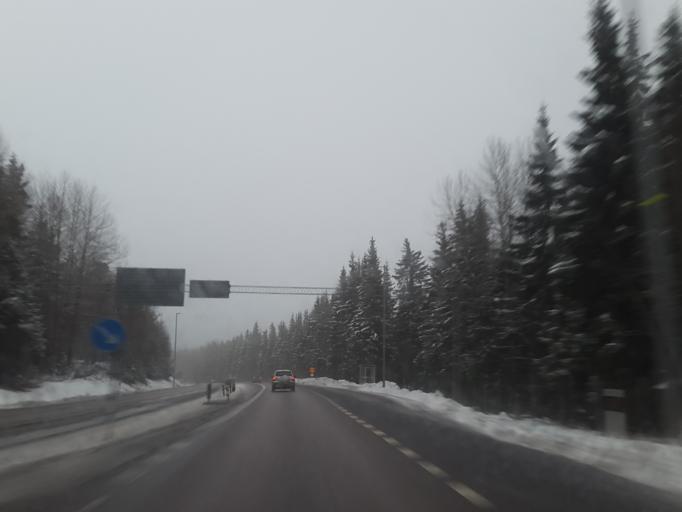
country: SE
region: Joenkoeping
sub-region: Mullsjo Kommun
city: Mullsjoe
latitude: 57.7673
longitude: 13.7221
